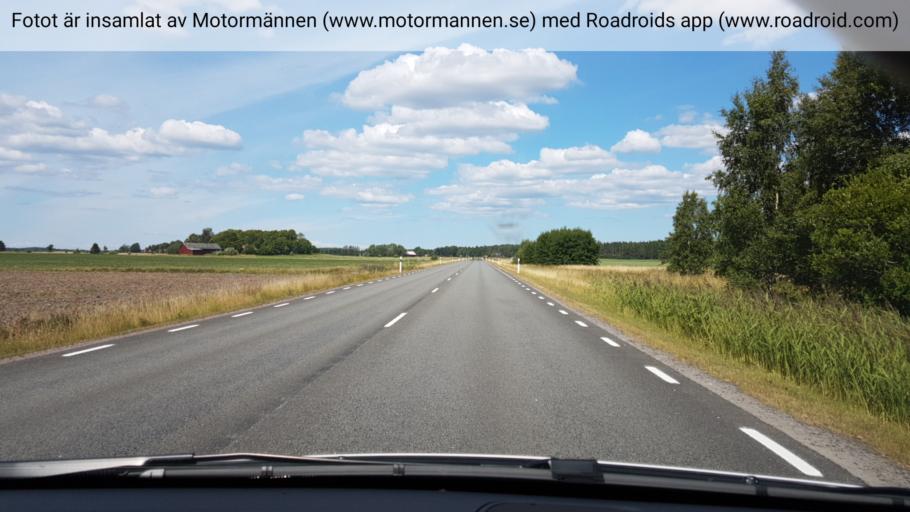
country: SE
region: Vaestra Goetaland
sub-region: Mariestads Kommun
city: Mariestad
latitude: 58.6372
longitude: 13.9170
